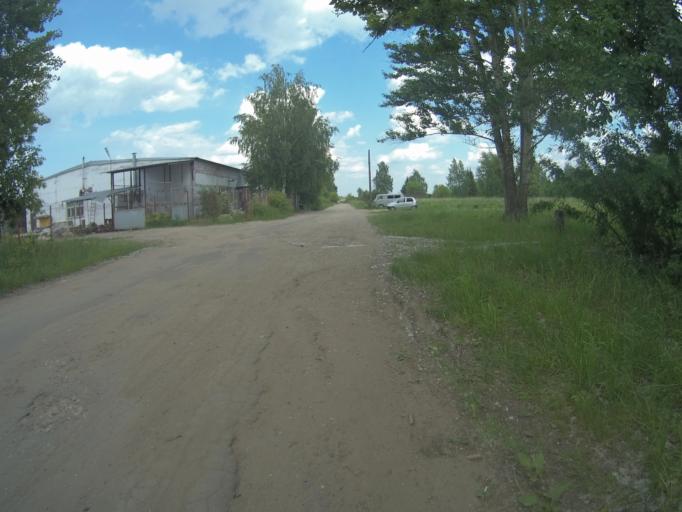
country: RU
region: Vladimir
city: Suzdal'
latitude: 56.4430
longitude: 40.4593
